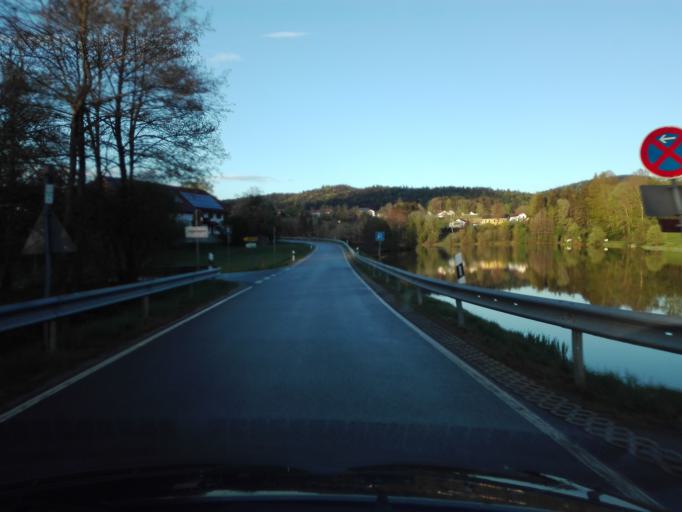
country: DE
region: Bavaria
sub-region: Lower Bavaria
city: Wegscheid
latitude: 48.5648
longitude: 13.7557
